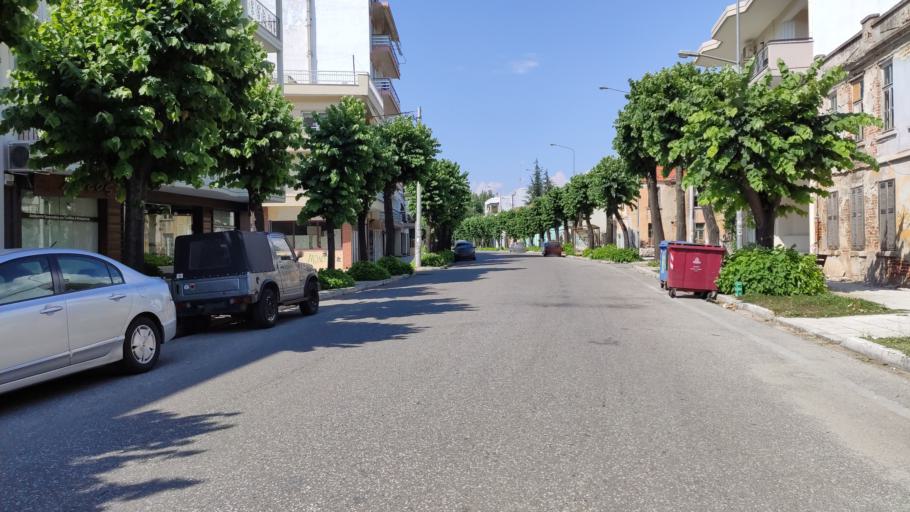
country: GR
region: East Macedonia and Thrace
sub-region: Nomos Rodopis
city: Komotini
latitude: 41.1113
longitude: 25.3963
